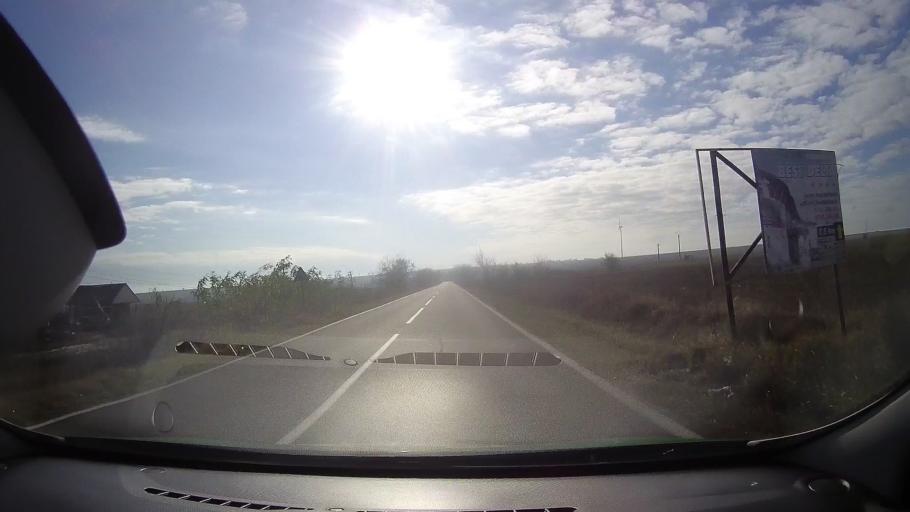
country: RO
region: Tulcea
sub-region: Comuna Mahmudia
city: Mahmudia
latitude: 45.0781
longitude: 29.0791
